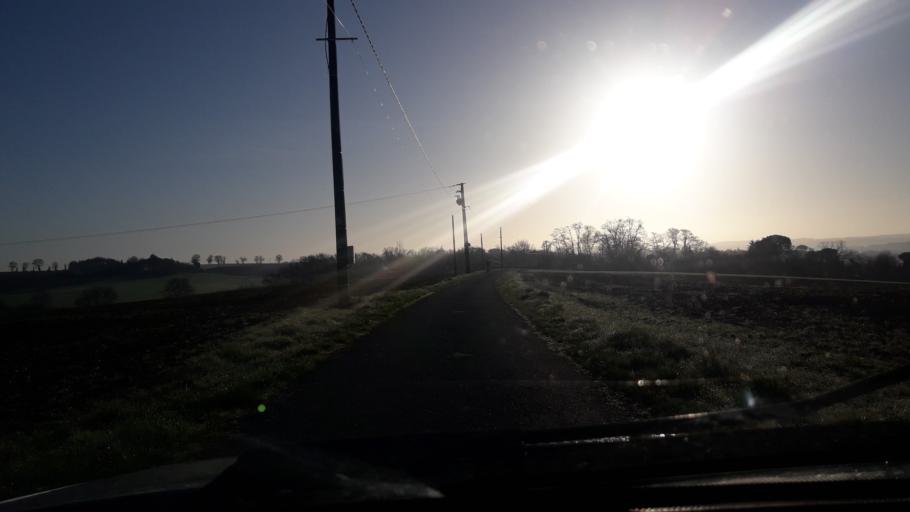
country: FR
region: Midi-Pyrenees
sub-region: Departement du Gers
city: Gimont
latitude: 43.6357
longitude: 0.9923
